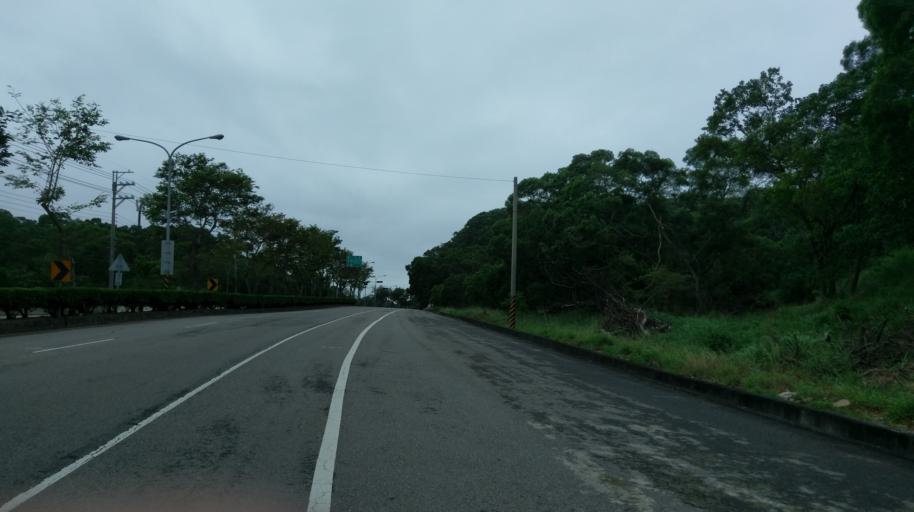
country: TW
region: Taiwan
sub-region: Miaoli
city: Miaoli
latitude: 24.6443
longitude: 120.8458
